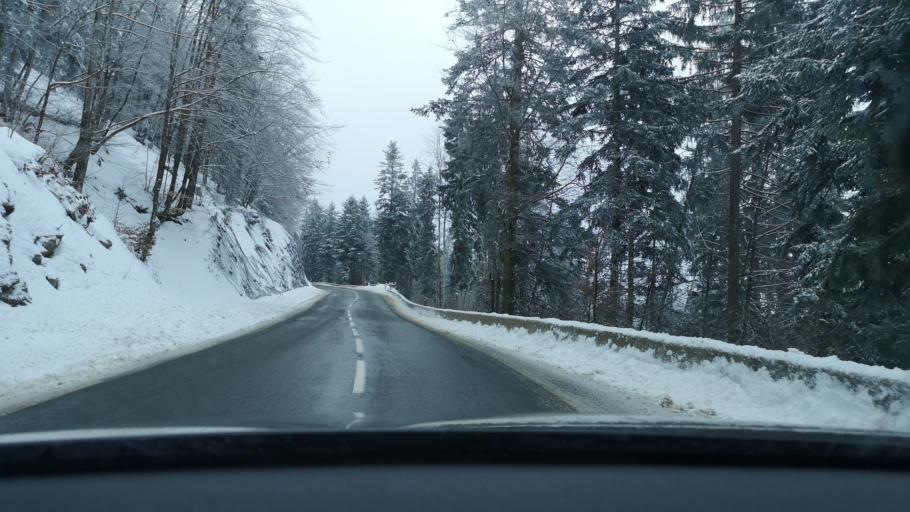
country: FR
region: Rhone-Alpes
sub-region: Departement de l'Ain
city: Oyonnax
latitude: 46.2330
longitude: 5.7020
